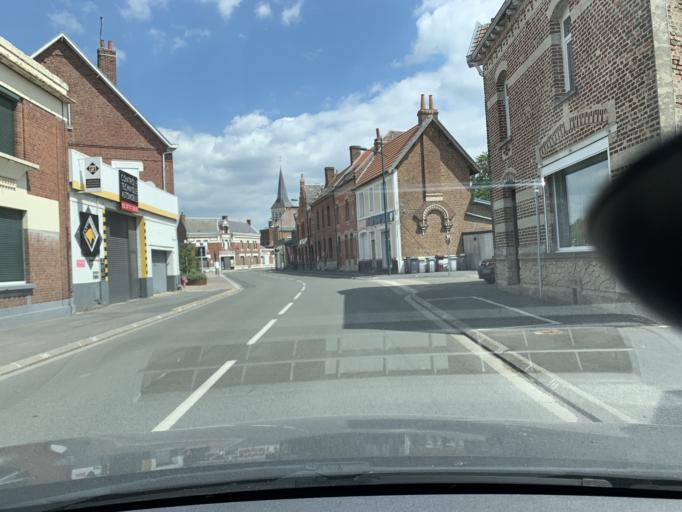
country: FR
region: Nord-Pas-de-Calais
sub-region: Departement du Nord
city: Arleux
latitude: 50.2792
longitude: 3.1029
